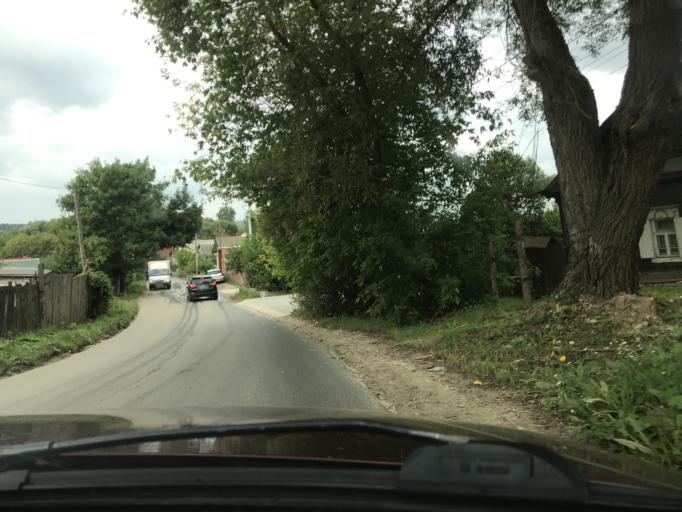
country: RU
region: Kaluga
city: Kaluga
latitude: 54.5379
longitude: 36.2441
